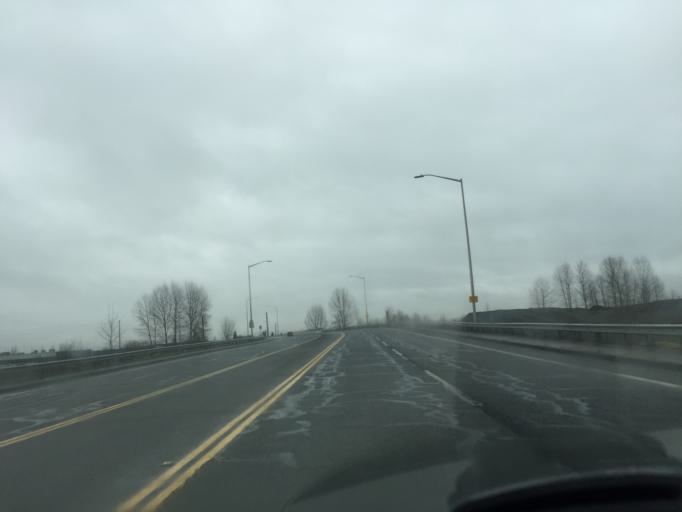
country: US
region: Washington
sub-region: King County
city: SeaTac
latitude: 47.4228
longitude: -122.2685
